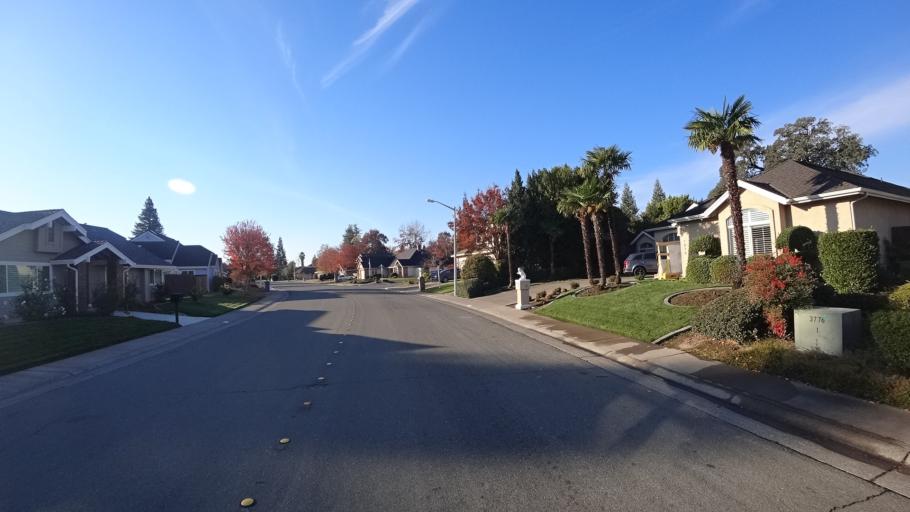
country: US
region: California
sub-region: Sacramento County
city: Citrus Heights
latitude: 38.7244
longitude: -121.2758
